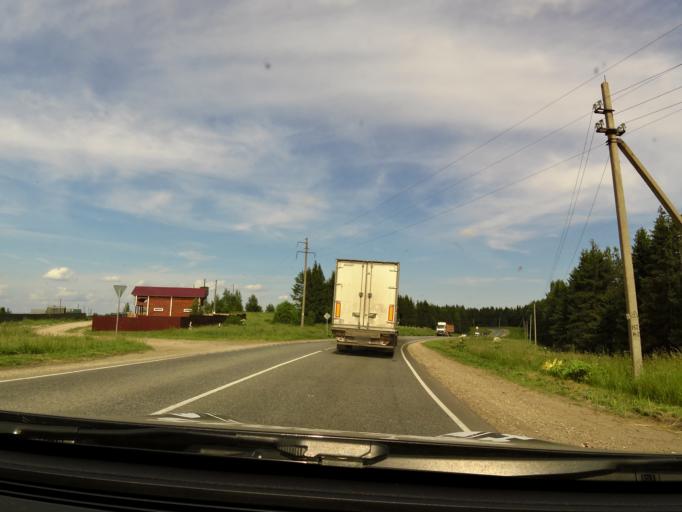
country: RU
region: Kirov
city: Slobodskoy
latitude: 58.7513
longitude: 50.3153
